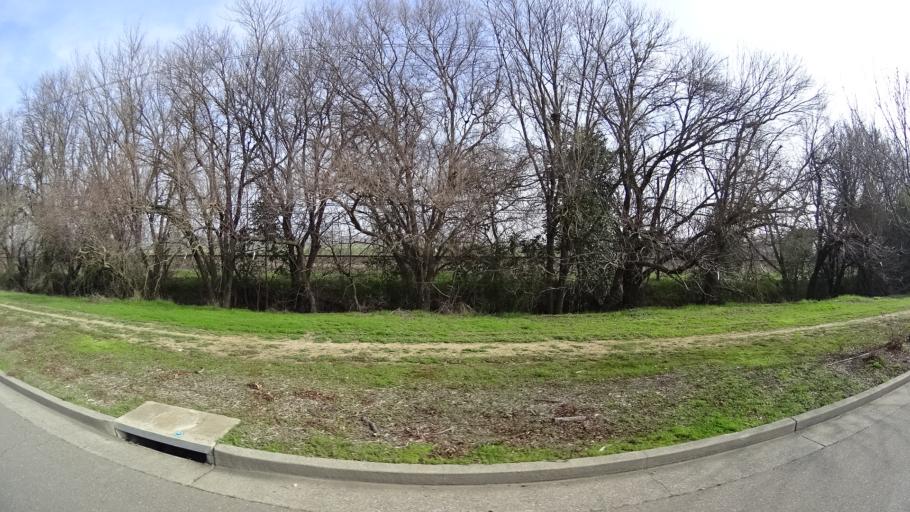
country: US
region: California
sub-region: Yolo County
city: Davis
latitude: 38.5688
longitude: -121.7461
